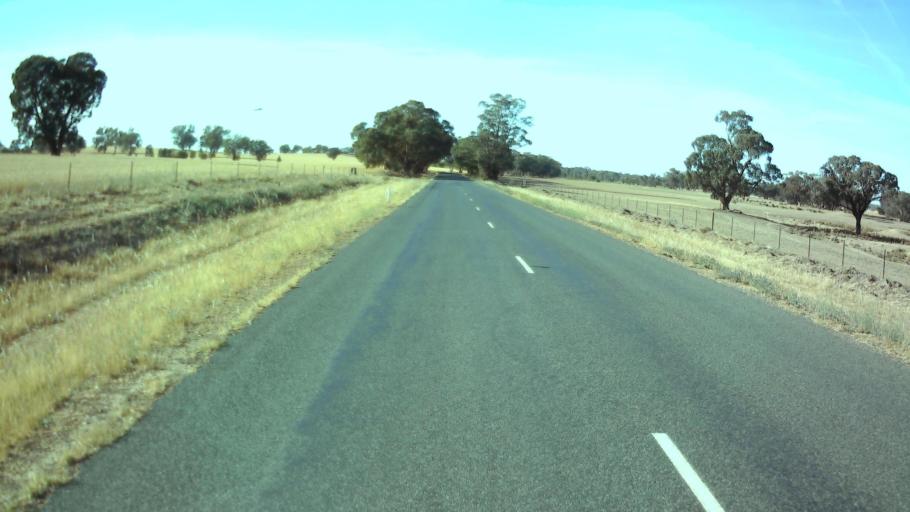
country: AU
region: New South Wales
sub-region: Weddin
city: Grenfell
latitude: -33.9724
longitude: 148.1408
